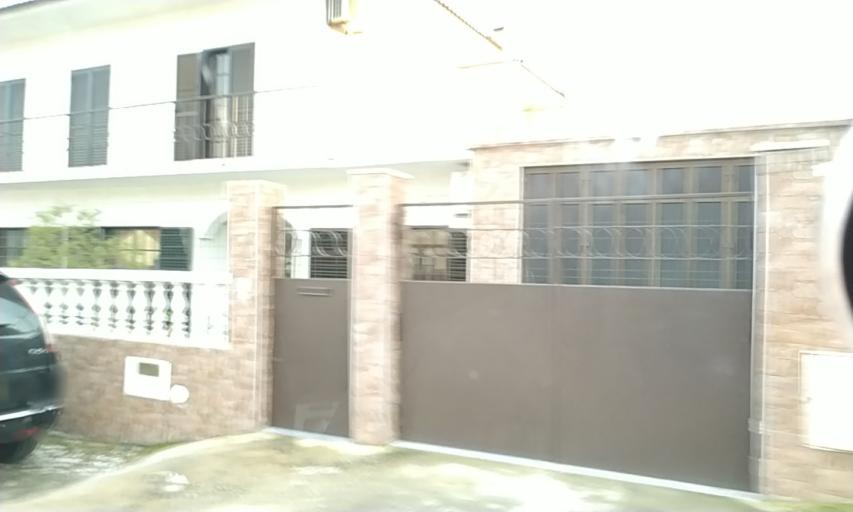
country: PT
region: Setubal
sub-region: Setubal
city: Setubal
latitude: 38.5260
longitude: -8.8629
